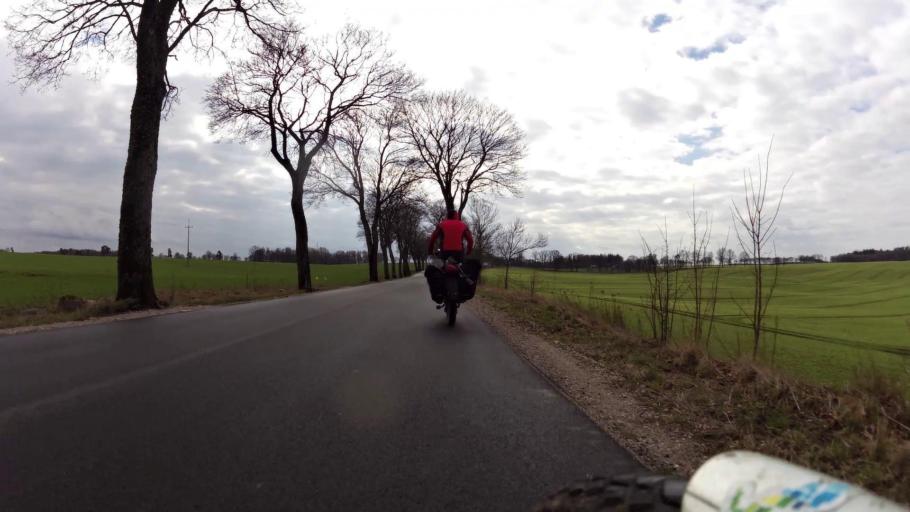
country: PL
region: Pomeranian Voivodeship
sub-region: Powiat bytowski
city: Kolczyglowy
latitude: 54.2286
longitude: 17.2419
